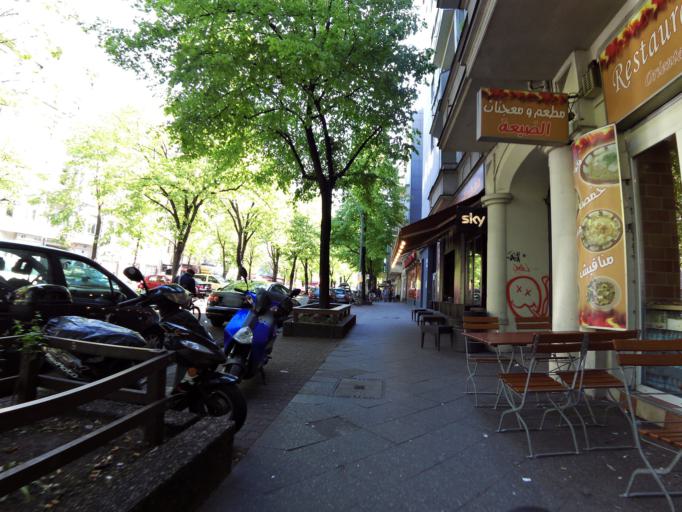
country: DE
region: Berlin
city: Berlin Treptow
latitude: 52.4855
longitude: 13.4319
